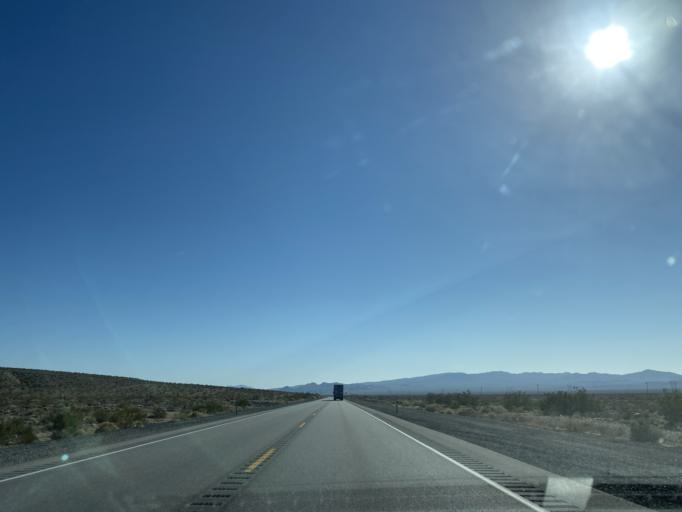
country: US
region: Nevada
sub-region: Nye County
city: Beatty
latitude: 36.8642
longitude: -116.7565
